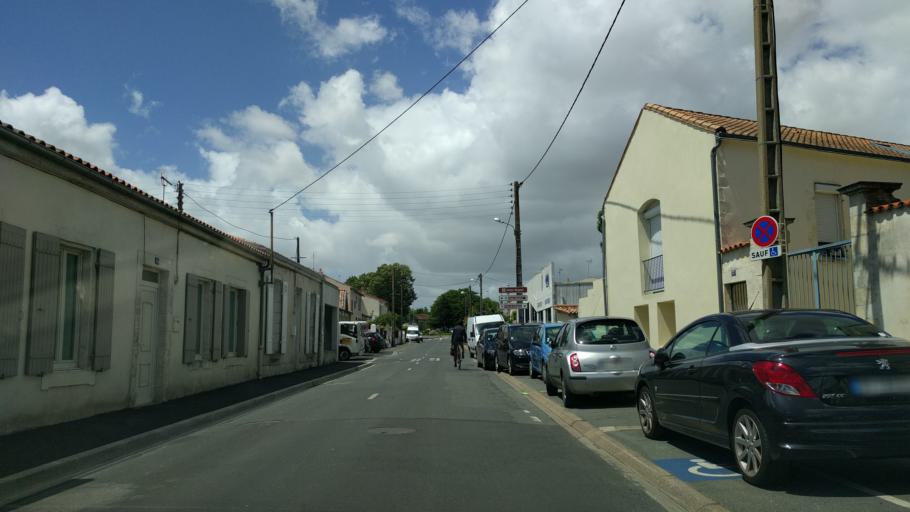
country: FR
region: Poitou-Charentes
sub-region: Departement de la Charente-Maritime
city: La Rochelle
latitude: 46.1610
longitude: -1.1377
